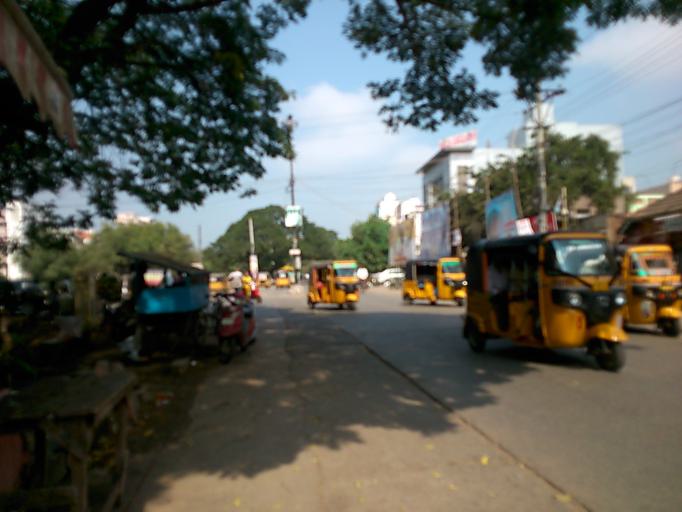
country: IN
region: Andhra Pradesh
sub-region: Guntur
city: Mangalagiri
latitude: 16.2425
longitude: 80.6471
